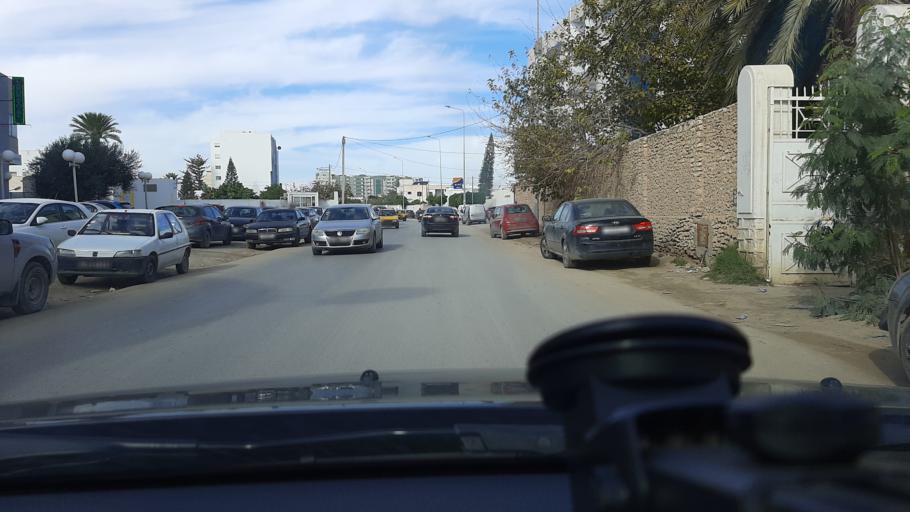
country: TN
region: Safaqis
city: Sfax
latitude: 34.7584
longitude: 10.7334
